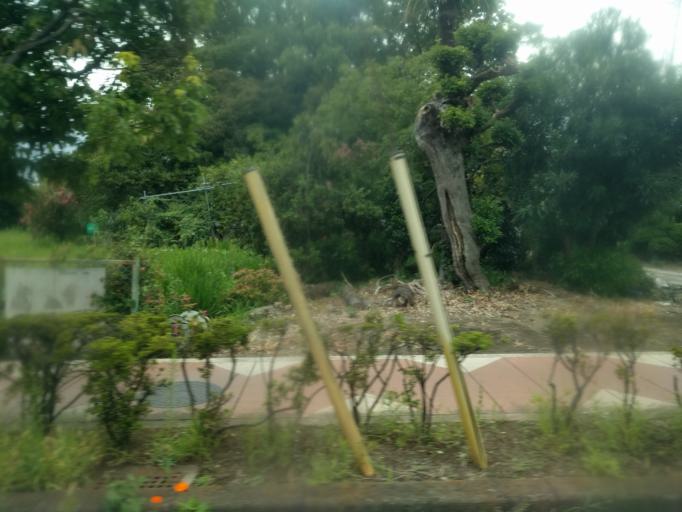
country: JP
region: Saitama
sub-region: Kawaguchi-shi
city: Hatogaya-honcho
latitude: 35.8255
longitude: 139.7338
